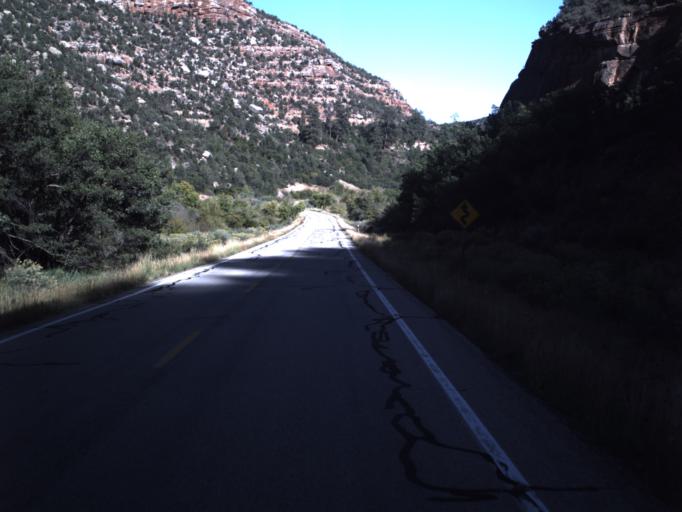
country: US
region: Utah
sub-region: Grand County
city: Moab
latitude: 38.3304
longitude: -109.0845
